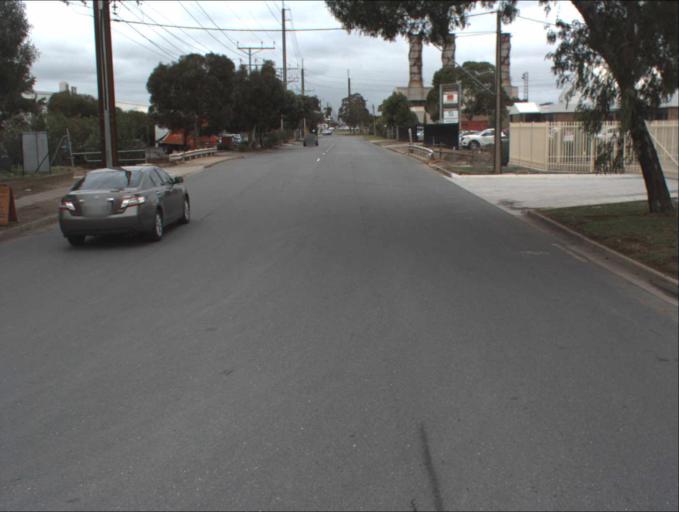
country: AU
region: South Australia
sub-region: Port Adelaide Enfield
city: Blair Athol
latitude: -34.8443
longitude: 138.5821
